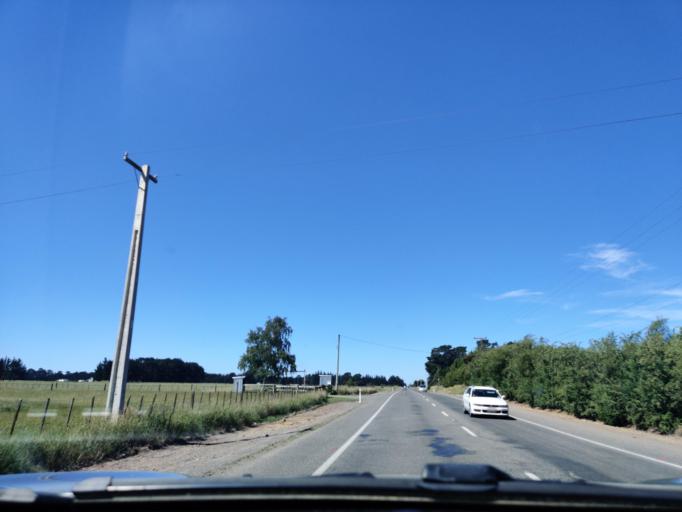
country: NZ
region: Wellington
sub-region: Masterton District
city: Masterton
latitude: -41.1059
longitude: 175.4096
